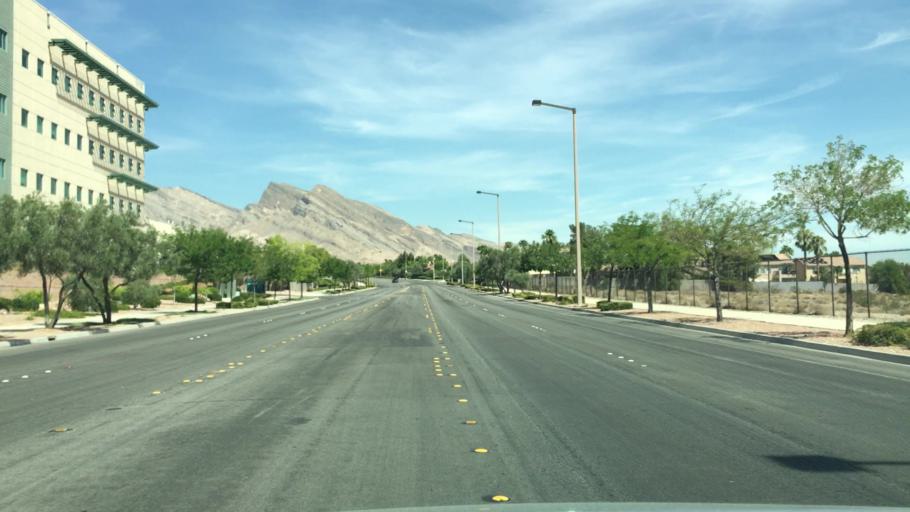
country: US
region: Nevada
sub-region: Clark County
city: Summerlin South
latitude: 36.1827
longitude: -115.3157
